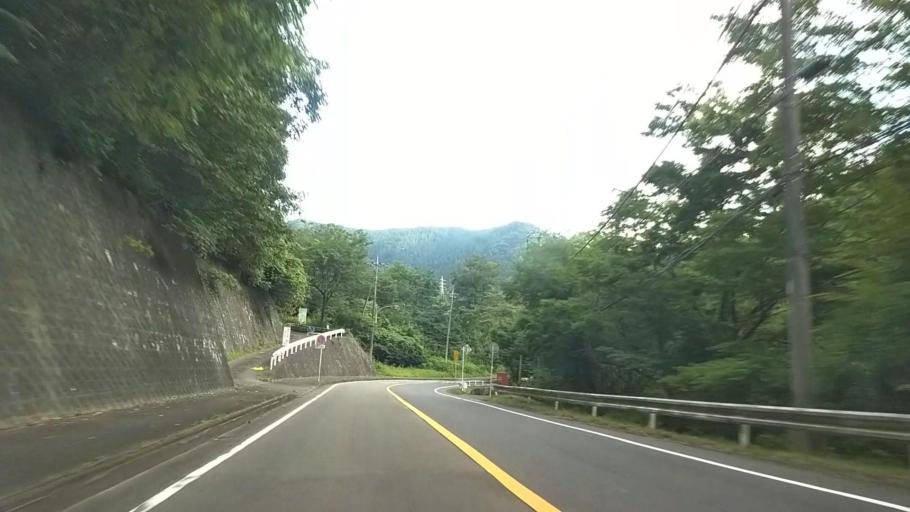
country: JP
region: Tokyo
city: Hachioji
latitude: 35.5610
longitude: 139.2360
